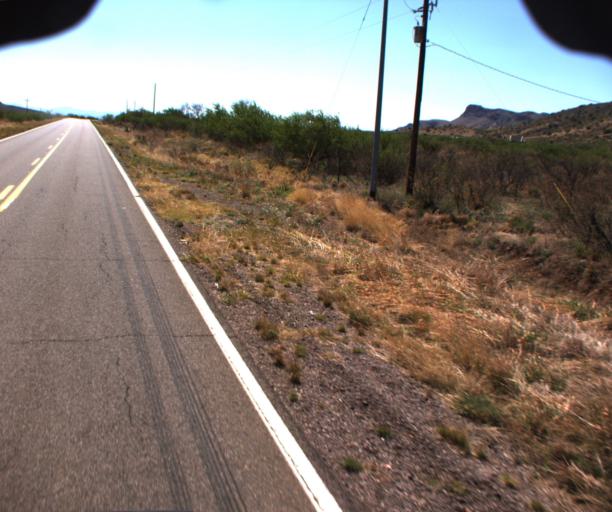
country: US
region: Arizona
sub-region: Cochise County
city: Douglas
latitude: 31.4870
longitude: -109.4173
